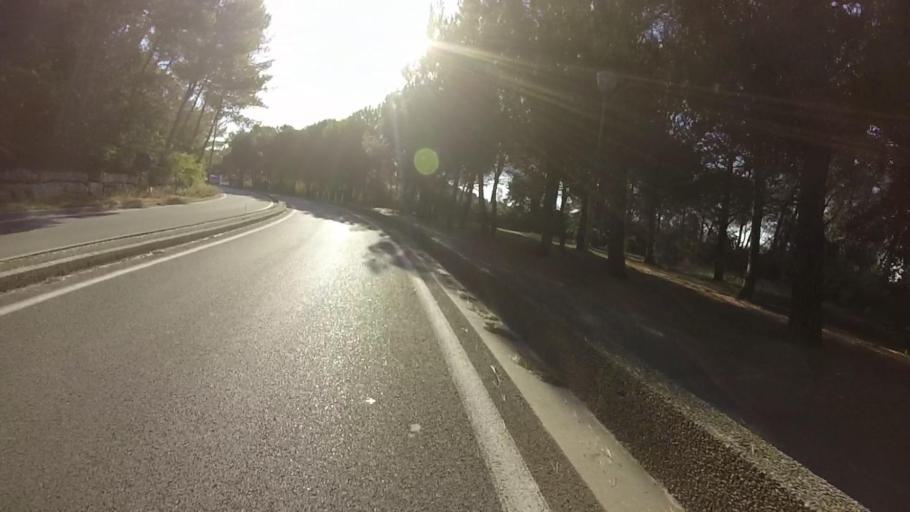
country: FR
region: Provence-Alpes-Cote d'Azur
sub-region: Departement des Alpes-Maritimes
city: Mougins
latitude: 43.6103
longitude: 7.0199
